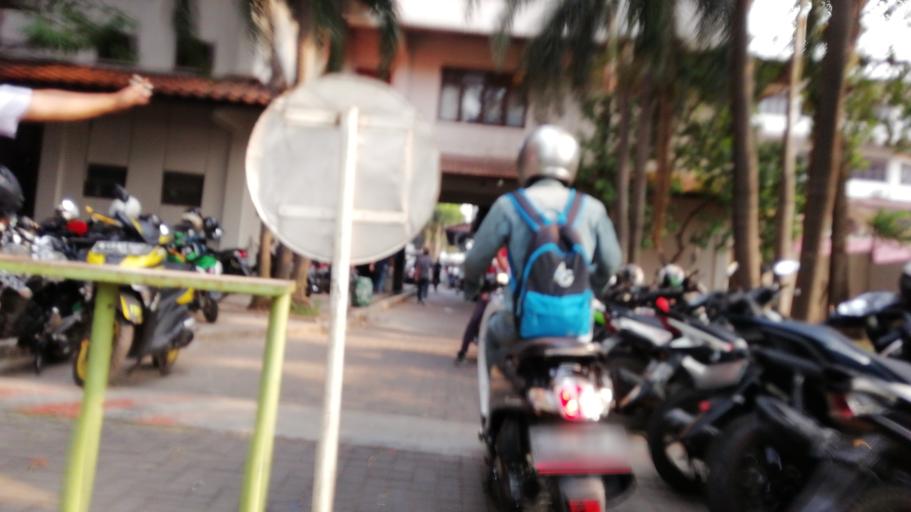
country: ID
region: West Java
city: Depok
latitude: -6.3532
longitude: 106.8414
